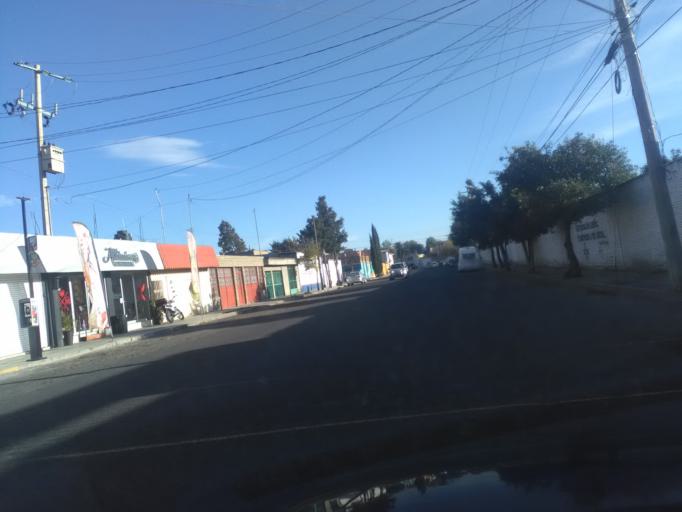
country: MX
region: Durango
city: Victoria de Durango
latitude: 24.0286
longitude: -104.6342
